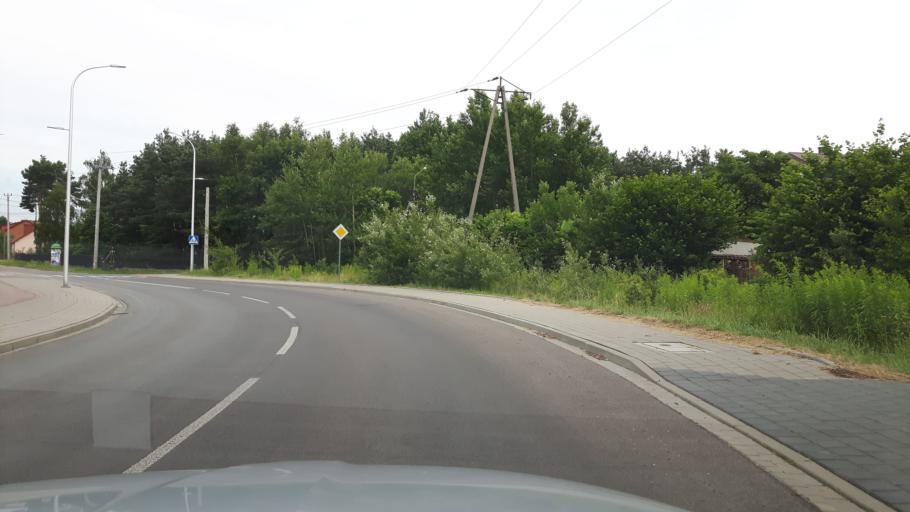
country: PL
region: Masovian Voivodeship
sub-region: Powiat wolominski
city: Wolomin
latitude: 52.3189
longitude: 21.2211
